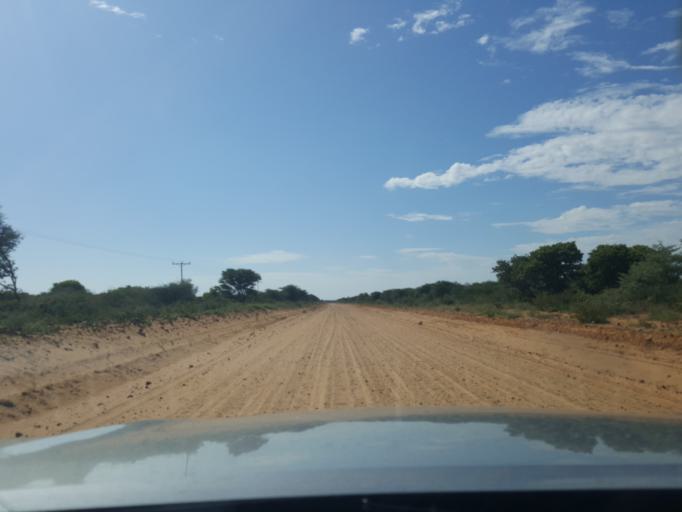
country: BW
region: Kweneng
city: Khudumelapye
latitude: -23.7150
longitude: 24.7326
